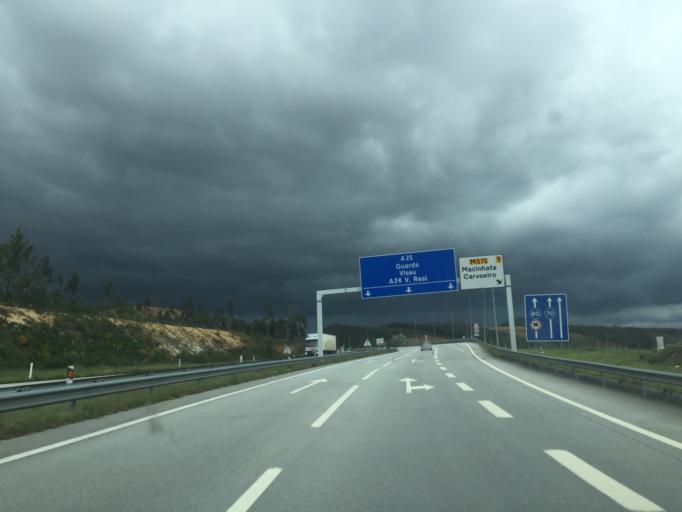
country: PT
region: Aveiro
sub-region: Albergaria-A-Velha
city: Albergaria-a-Velha
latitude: 40.6777
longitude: -8.4368
